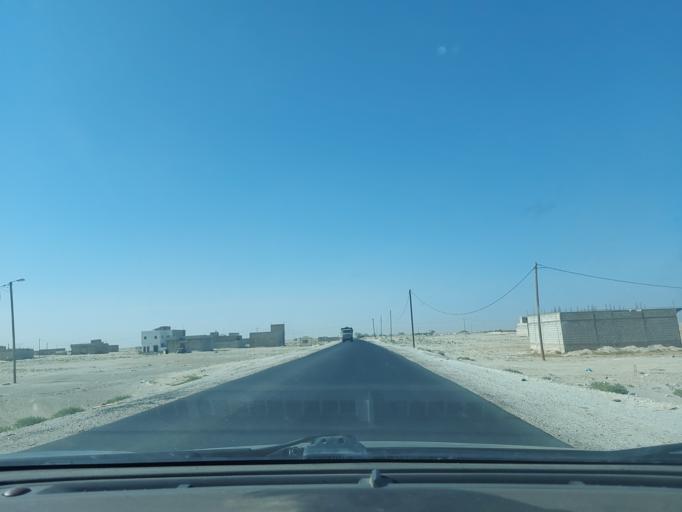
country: MR
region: Nouakchott
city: Nouakchott
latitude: 17.9962
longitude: -15.9882
